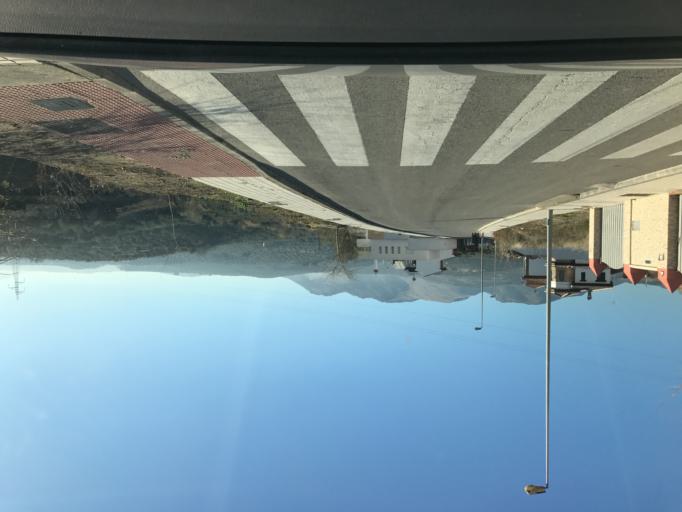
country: ES
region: Andalusia
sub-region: Provincia de Granada
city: Peligros
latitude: 37.2344
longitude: -3.6176
